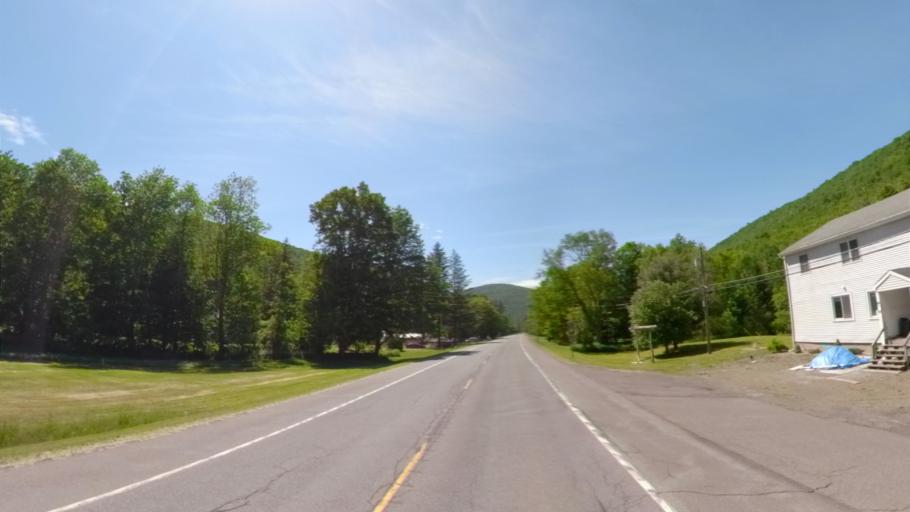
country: US
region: New York
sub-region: Ulster County
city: Shokan
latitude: 42.1175
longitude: -74.4573
